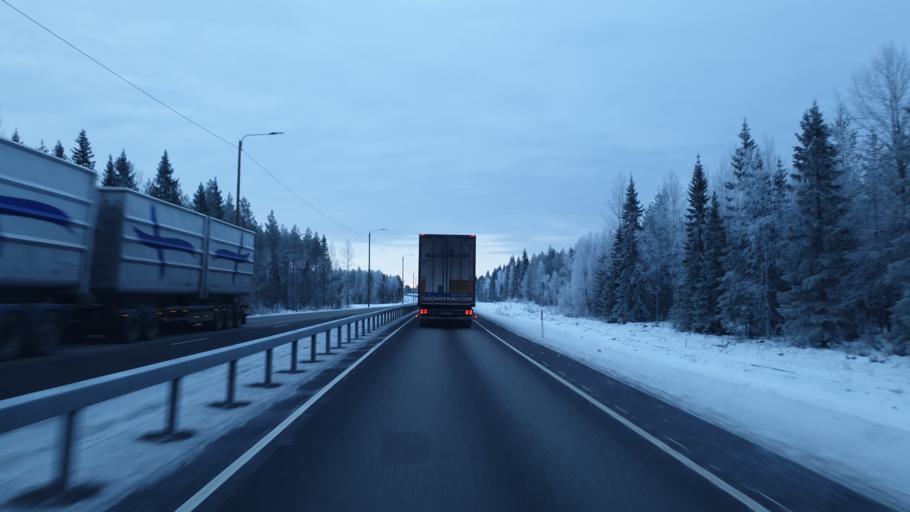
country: FI
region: Northern Ostrobothnia
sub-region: Oulunkaari
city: Kuivaniemi
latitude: 65.6171
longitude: 25.1626
